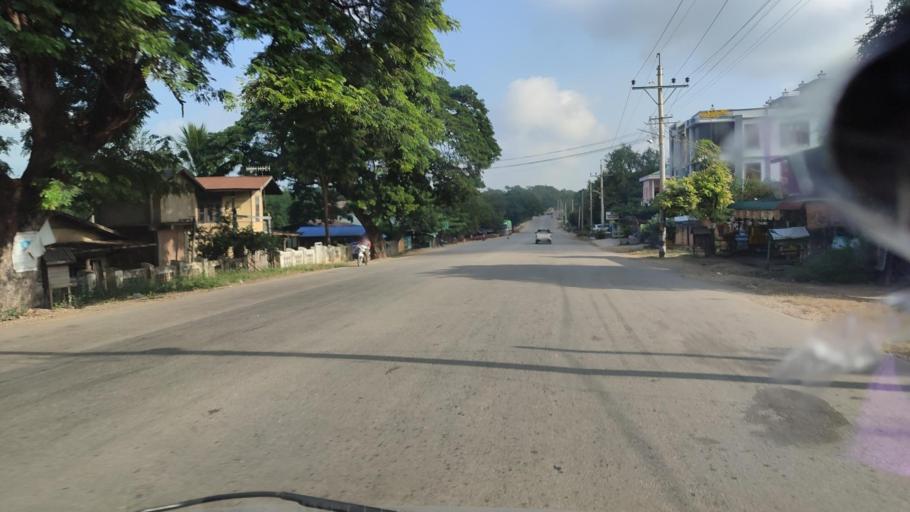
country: MM
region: Mandalay
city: Yamethin
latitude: 20.7616
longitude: 96.3192
